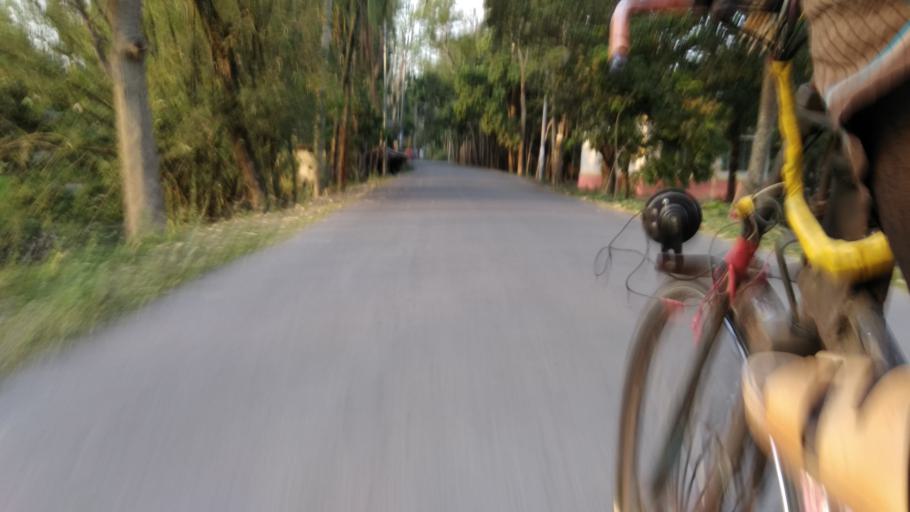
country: BD
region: Barisal
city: Mehendiganj
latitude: 22.9344
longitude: 90.4061
